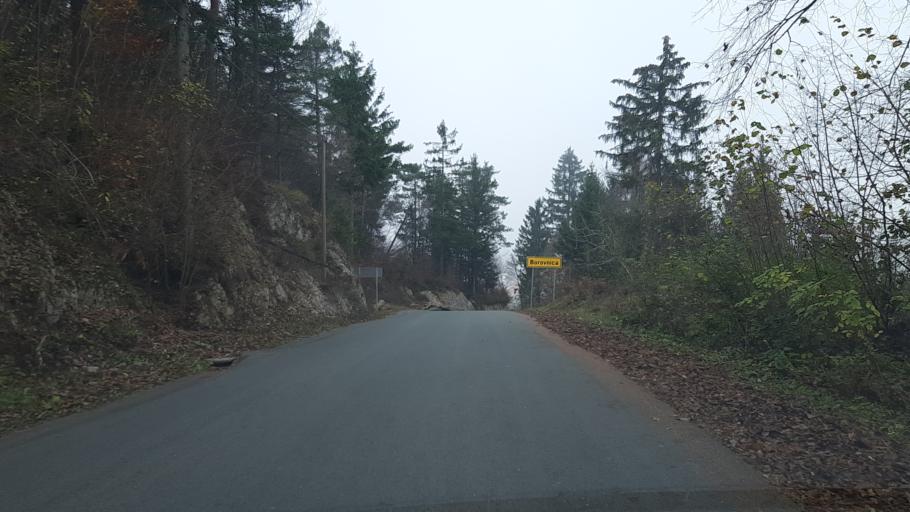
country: SI
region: Borovnica
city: Borovnica
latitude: 45.9107
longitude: 14.3664
